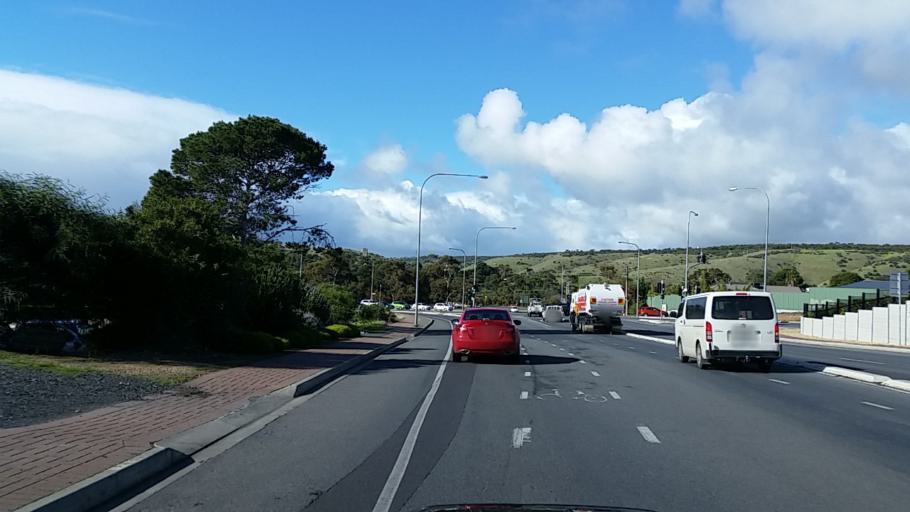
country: AU
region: South Australia
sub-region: Onkaparinga
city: Noarlunga
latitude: -35.1802
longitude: 138.4946
